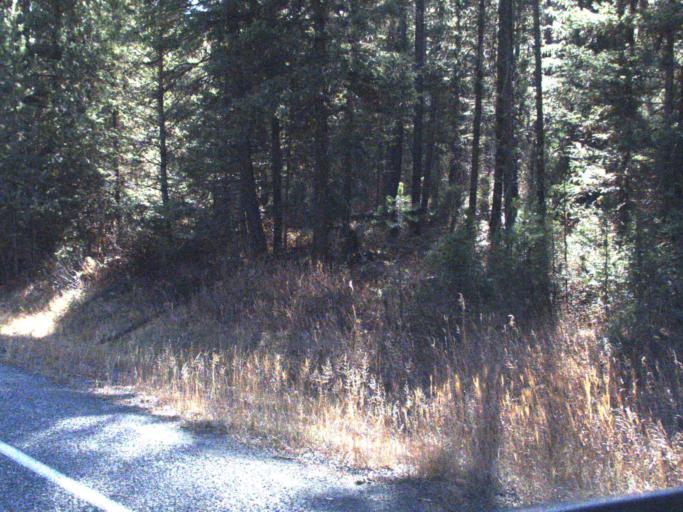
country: US
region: Washington
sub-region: Ferry County
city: Republic
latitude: 48.6602
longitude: -118.8201
